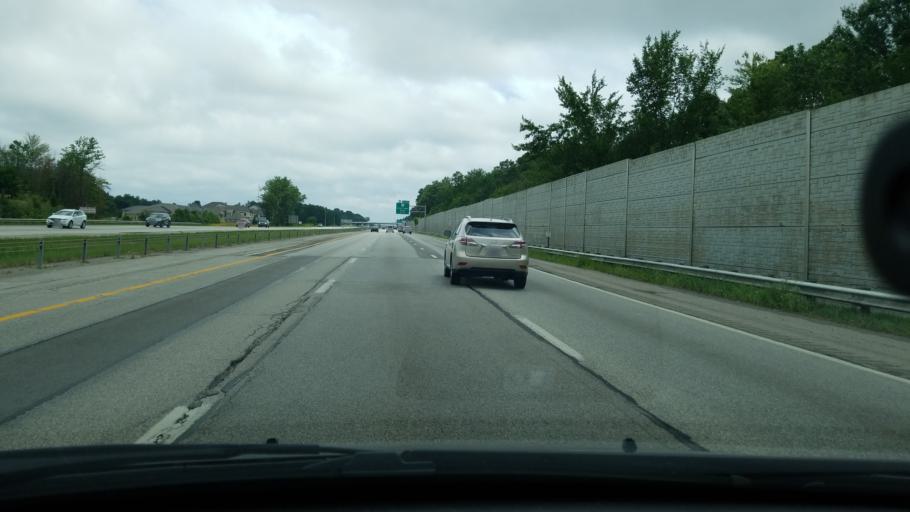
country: US
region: Ohio
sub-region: Lorain County
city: Avon
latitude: 41.4644
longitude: -82.0347
